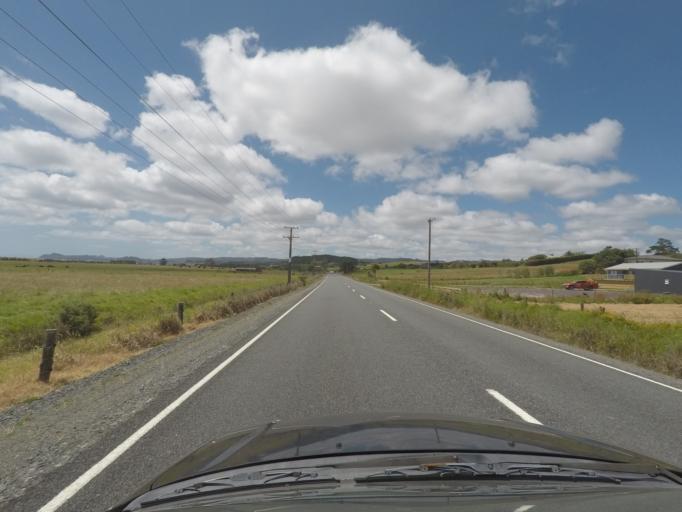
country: NZ
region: Northland
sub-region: Whangarei
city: Ruakaka
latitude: -36.0077
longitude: 174.4798
